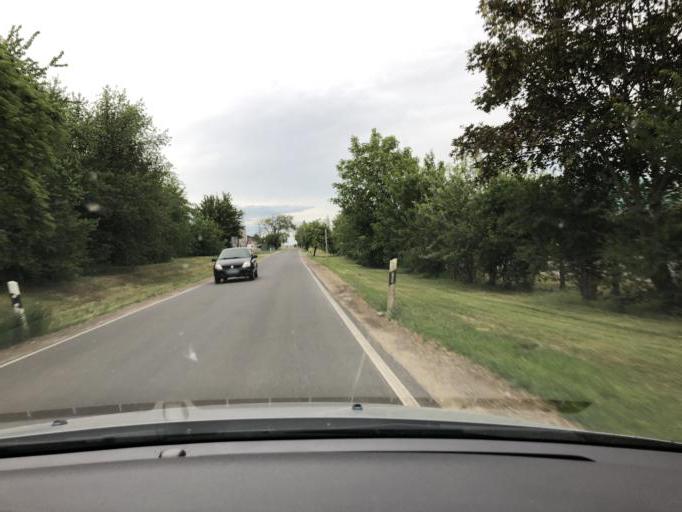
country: DE
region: Thuringia
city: Pfiffelbach
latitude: 51.0662
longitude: 11.4437
